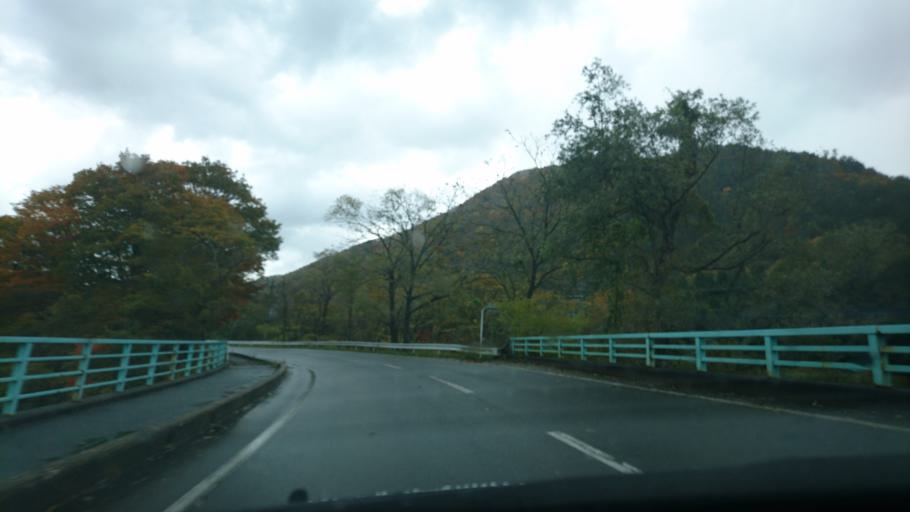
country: JP
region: Iwate
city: Shizukuishi
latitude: 39.6118
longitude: 140.9434
